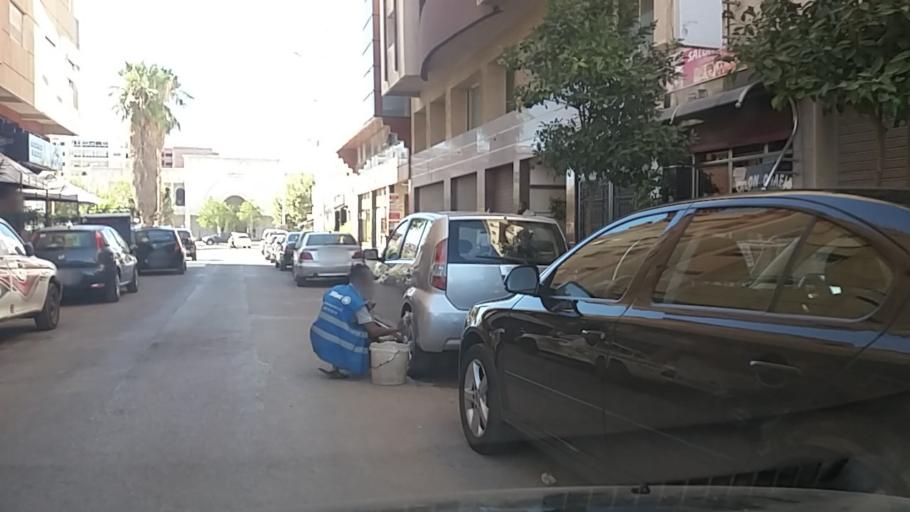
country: MA
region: Gharb-Chrarda-Beni Hssen
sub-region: Kenitra Province
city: Kenitra
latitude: 34.2608
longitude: -6.5792
